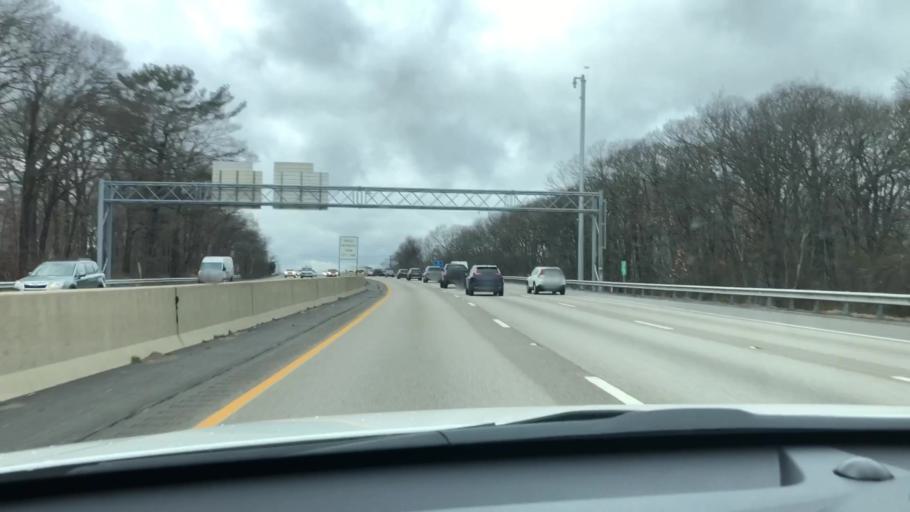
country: US
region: Massachusetts
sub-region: Norfolk County
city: Weymouth
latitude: 42.1986
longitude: -70.9667
